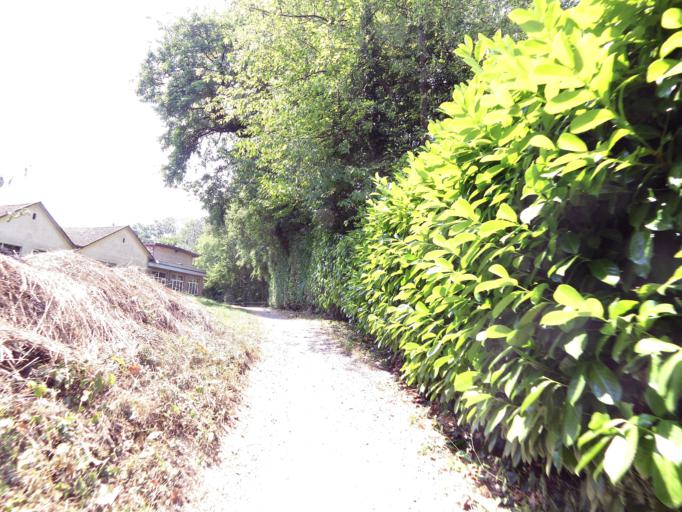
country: CH
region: Aargau
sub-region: Bezirk Baden
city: Wurenlos
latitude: 47.4342
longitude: 8.3711
